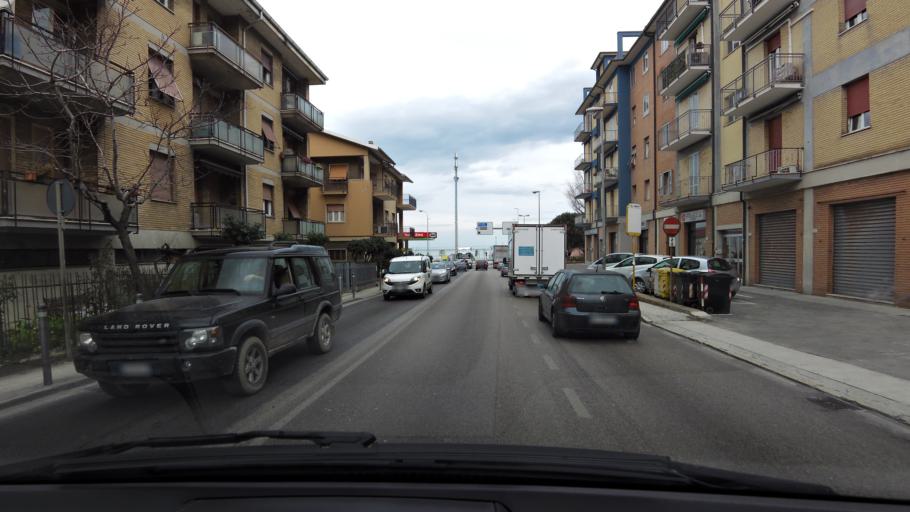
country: IT
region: The Marches
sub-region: Provincia di Ancona
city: Posatora
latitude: 43.6086
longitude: 13.4557
